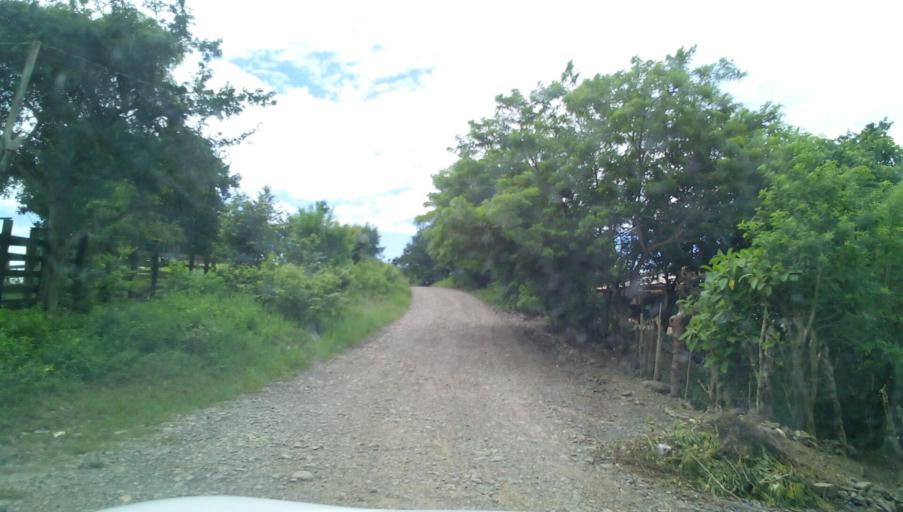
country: MX
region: Veracruz
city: Tepetzintla
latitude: 21.1492
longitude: -97.8560
